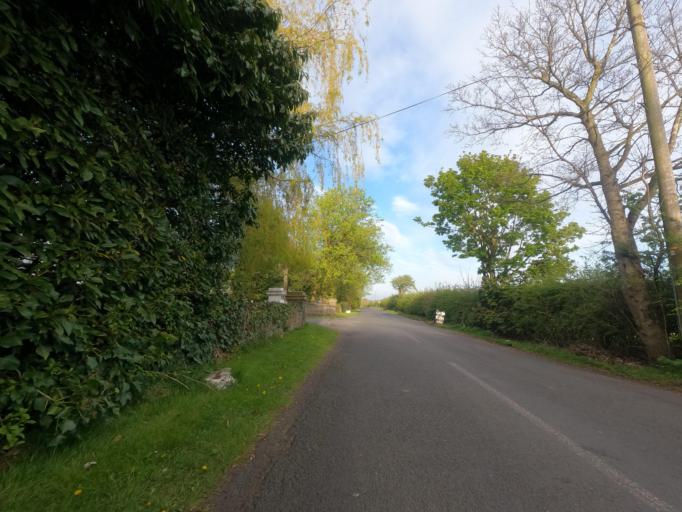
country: GB
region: England
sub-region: Northumberland
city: Cramlington
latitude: 55.0698
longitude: -1.6164
